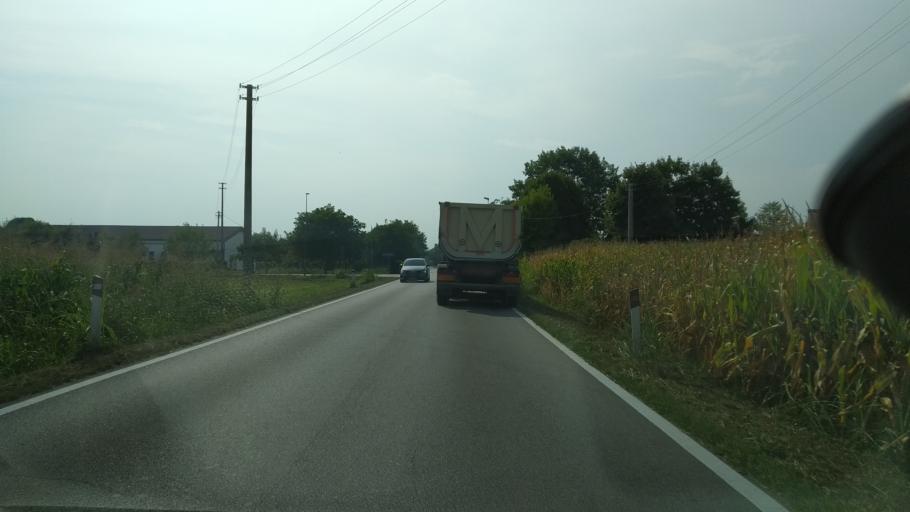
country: IT
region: Veneto
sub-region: Provincia di Padova
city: Fontaniva
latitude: 45.6604
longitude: 11.7415
